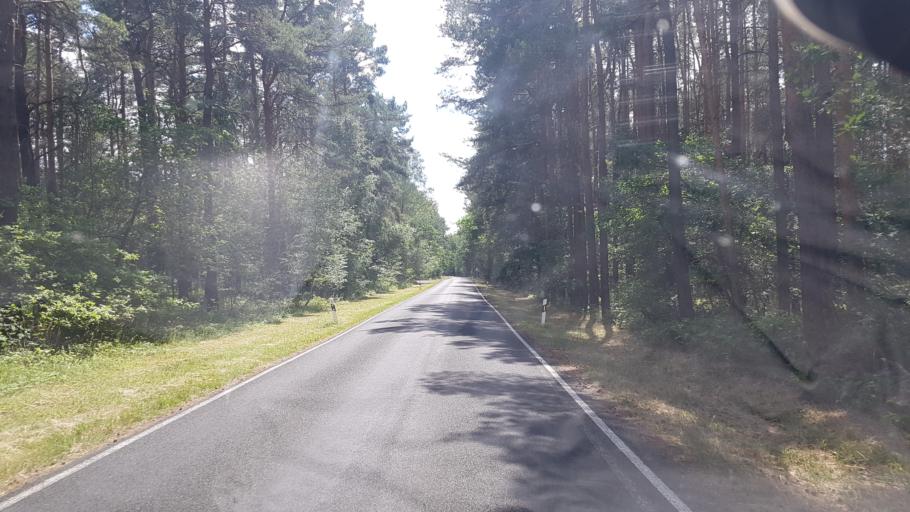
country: DE
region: Brandenburg
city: Sallgast
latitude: 51.5839
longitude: 13.9199
